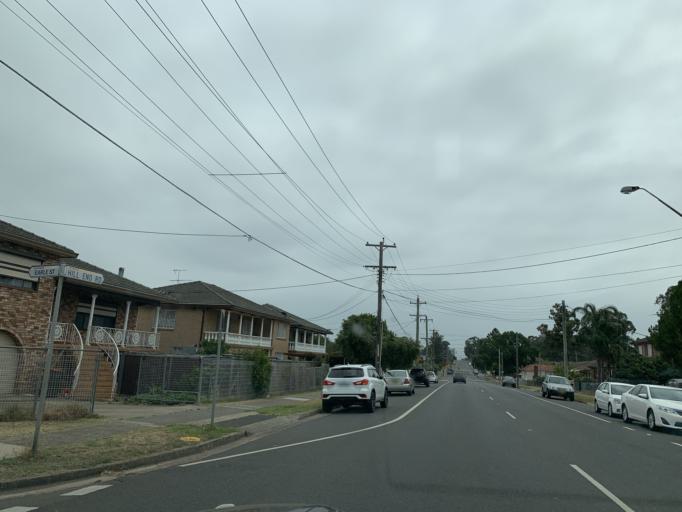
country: AU
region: New South Wales
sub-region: Blacktown
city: Doonside
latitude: -33.7611
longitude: 150.8698
